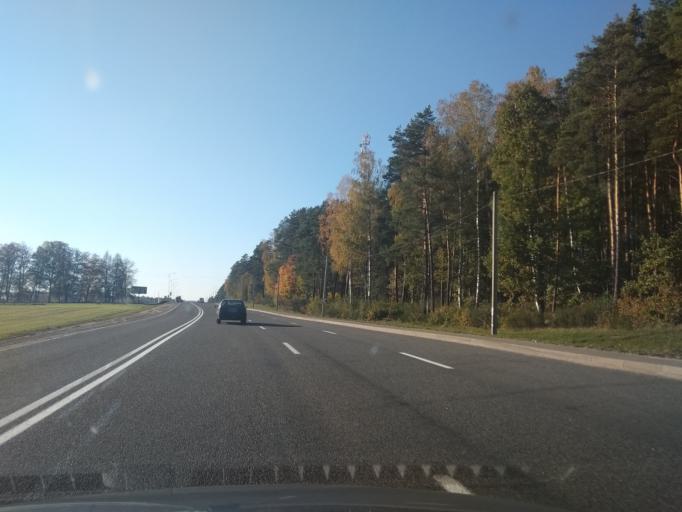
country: BY
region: Grodnenskaya
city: Vyalikaya Byerastavitsa
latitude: 53.1204
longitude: 23.9182
